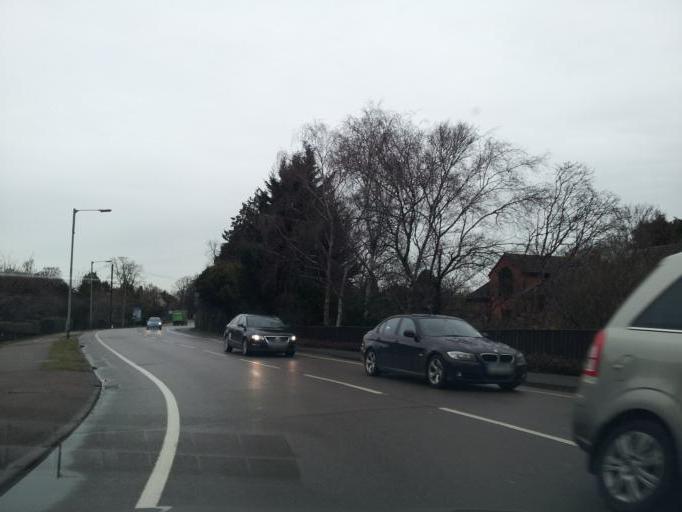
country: GB
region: England
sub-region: Cambridgeshire
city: Cambridge
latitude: 52.1769
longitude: 0.1445
